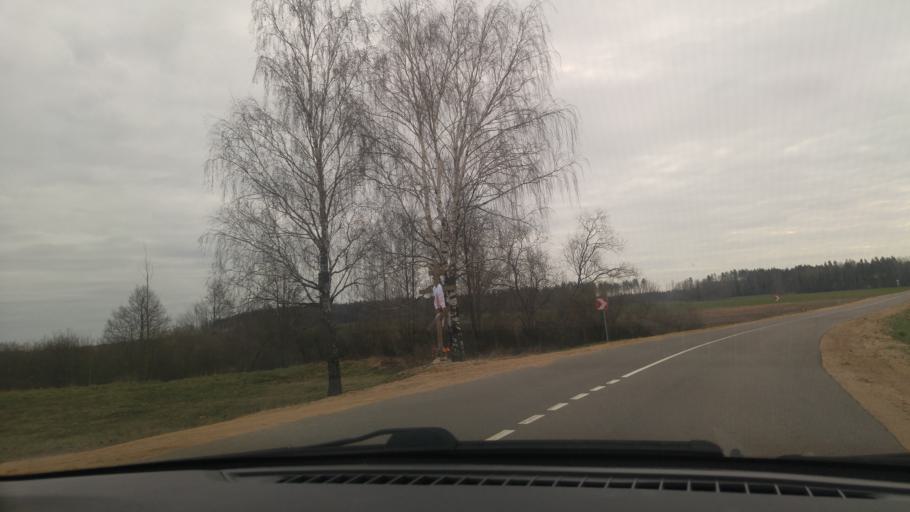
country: BY
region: Minsk
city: Chervyen'
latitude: 53.7314
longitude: 28.2794
